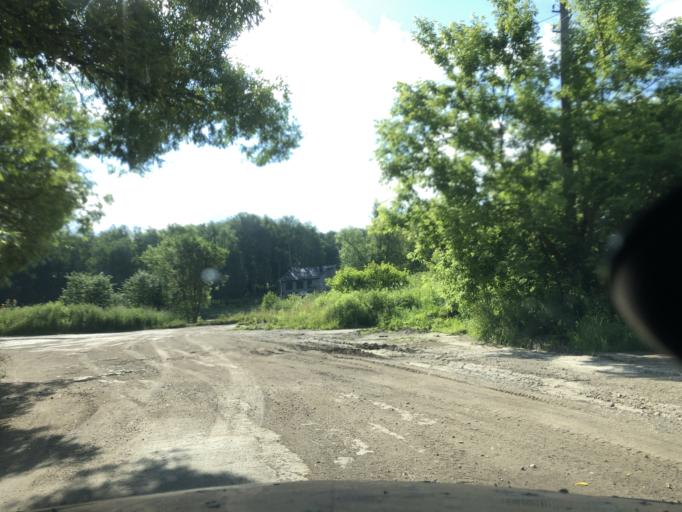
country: RU
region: Tula
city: Shvartsevskiy
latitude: 54.2519
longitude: 37.9280
